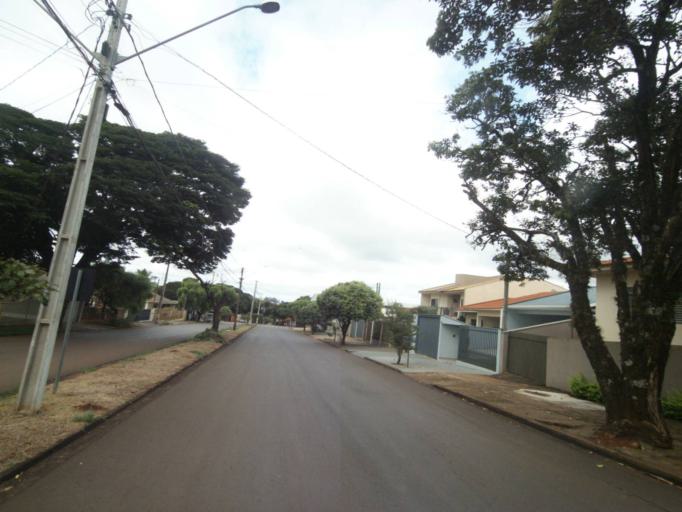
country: BR
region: Parana
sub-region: Campo Mourao
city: Campo Mourao
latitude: -24.0489
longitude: -52.3766
